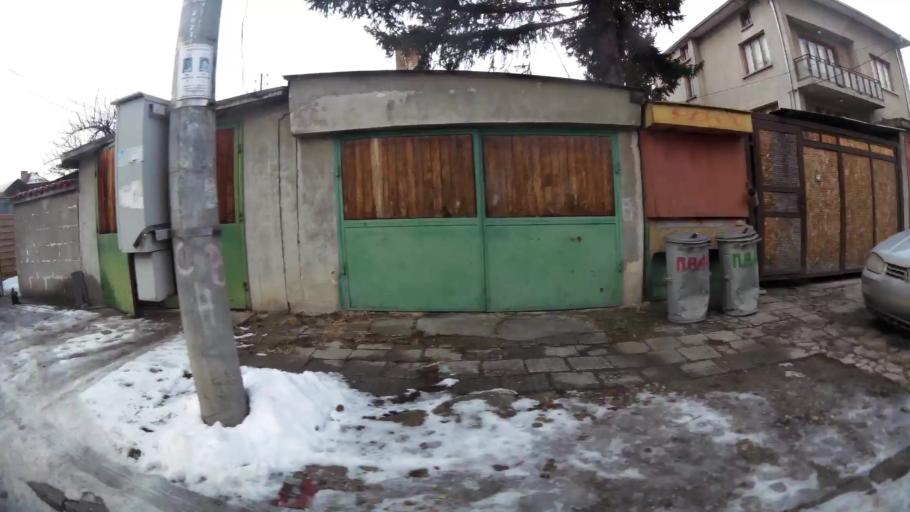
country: BG
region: Sofia-Capital
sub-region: Stolichna Obshtina
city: Sofia
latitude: 42.7242
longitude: 23.3340
